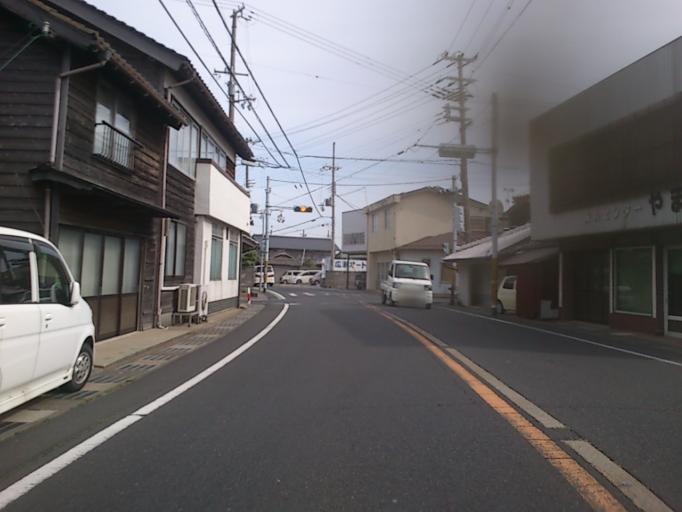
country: JP
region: Kyoto
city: Miyazu
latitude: 35.6849
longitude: 135.0244
